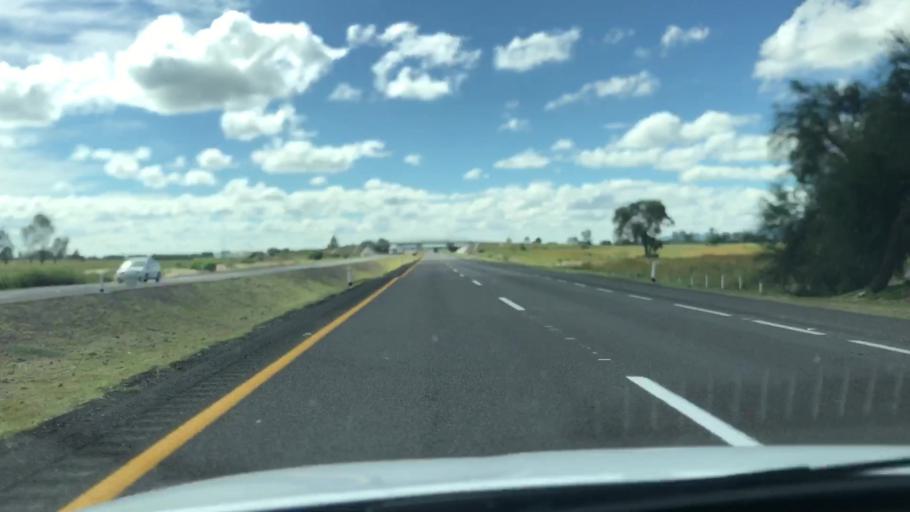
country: MX
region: Guanajuato
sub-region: Silao de la Victoria
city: La Aldea
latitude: 20.9197
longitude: -101.4949
